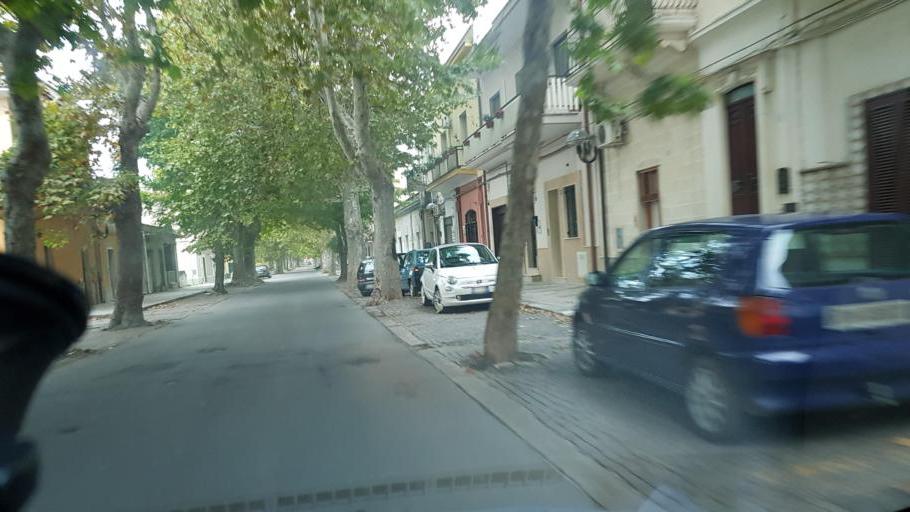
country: IT
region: Apulia
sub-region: Provincia di Brindisi
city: Oria
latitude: 40.5035
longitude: 17.6454
